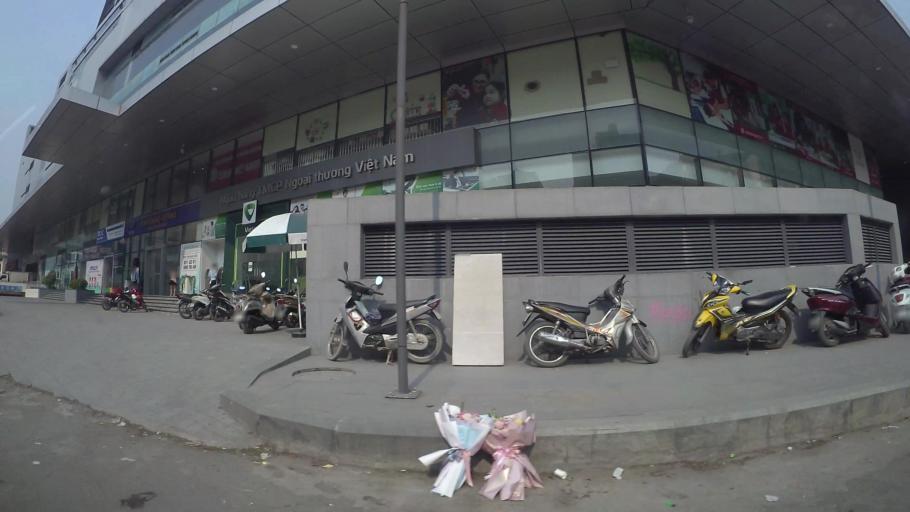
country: VN
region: Ha Noi
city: Dong Da
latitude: 20.9995
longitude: 105.8282
